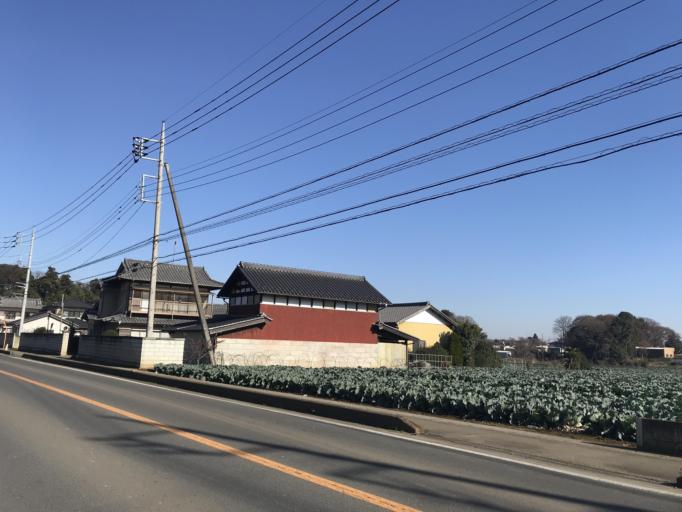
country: JP
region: Tochigi
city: Oyama
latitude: 36.2235
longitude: 139.8239
